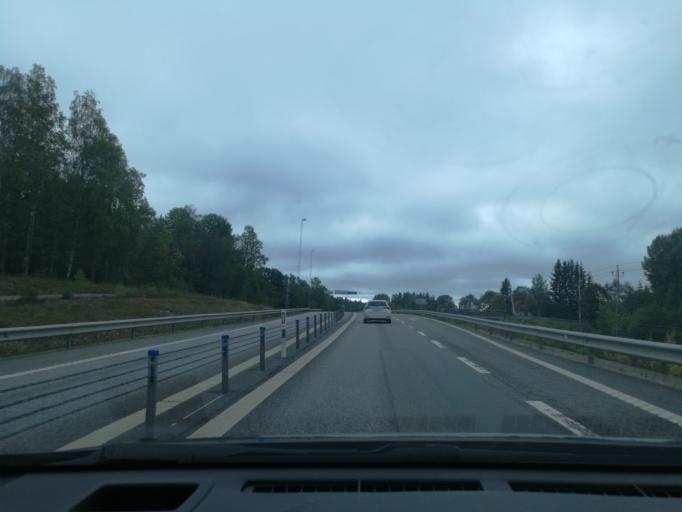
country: SE
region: OEstergoetland
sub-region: Norrkopings Kommun
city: Jursla
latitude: 58.7836
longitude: 16.1578
